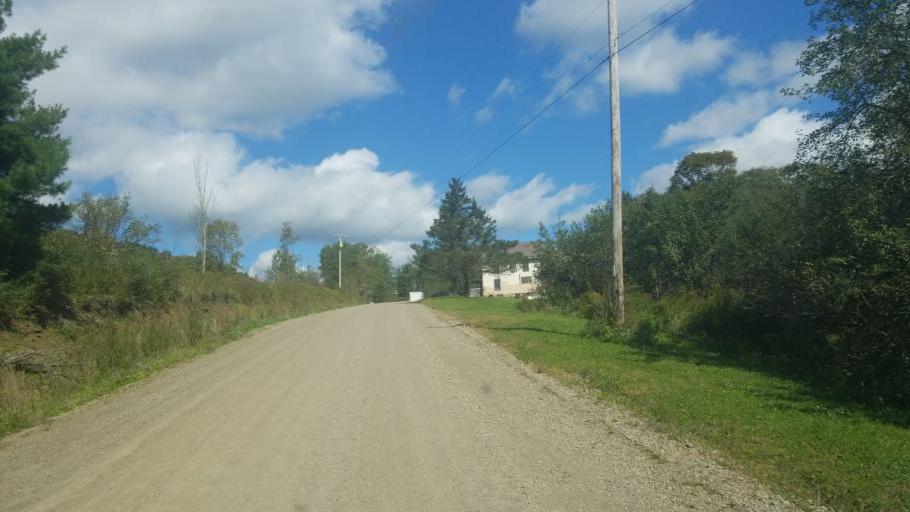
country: US
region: New York
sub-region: Allegany County
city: Cuba
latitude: 42.1736
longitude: -78.3318
